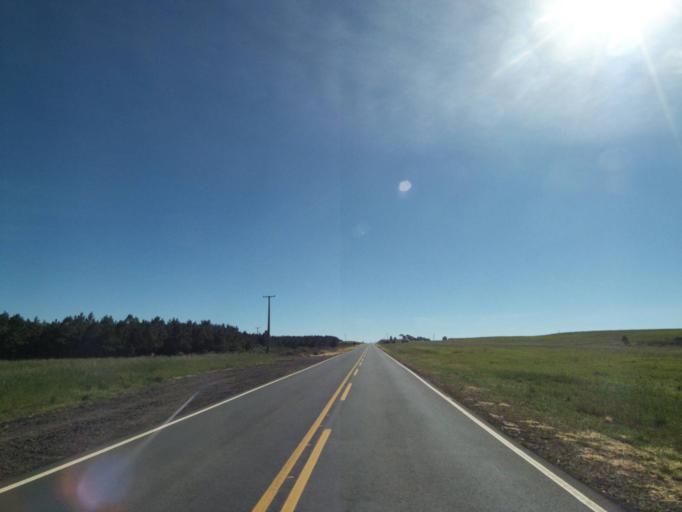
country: BR
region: Parana
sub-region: Castro
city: Castro
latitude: -24.6996
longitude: -50.1941
